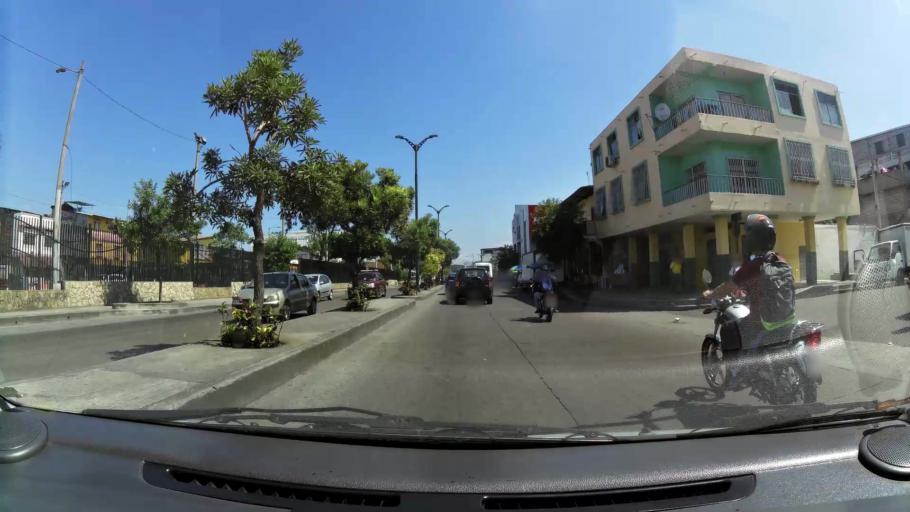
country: EC
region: Guayas
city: Guayaquil
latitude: -2.2095
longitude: -79.9292
